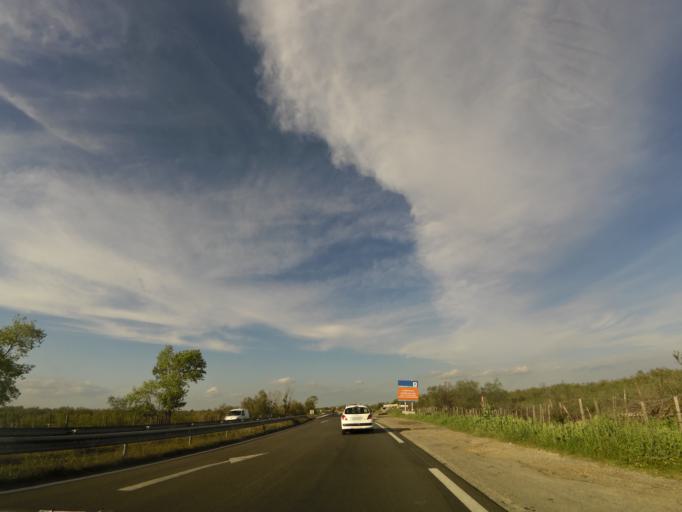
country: FR
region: Languedoc-Roussillon
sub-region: Departement de l'Herault
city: La Grande-Motte
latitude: 43.5790
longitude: 4.1013
